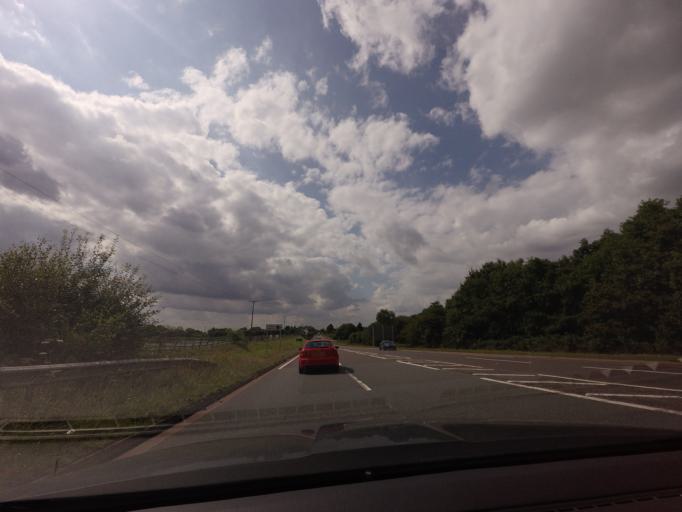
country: GB
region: England
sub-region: Staffordshire
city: Penkridge
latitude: 52.6895
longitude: -2.1068
